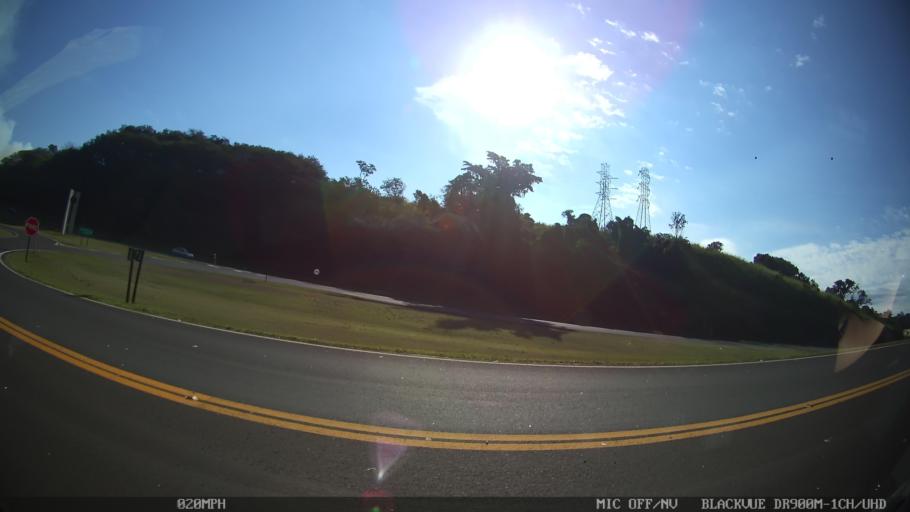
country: BR
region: Sao Paulo
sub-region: Piracicaba
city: Piracicaba
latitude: -22.6883
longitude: -47.5833
